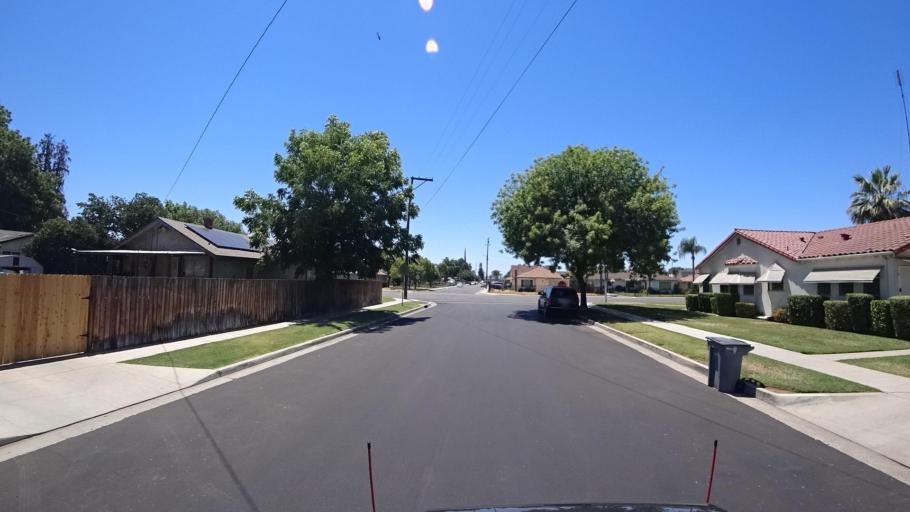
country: US
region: California
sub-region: Fresno County
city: Fresno
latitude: 36.7436
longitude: -119.7387
